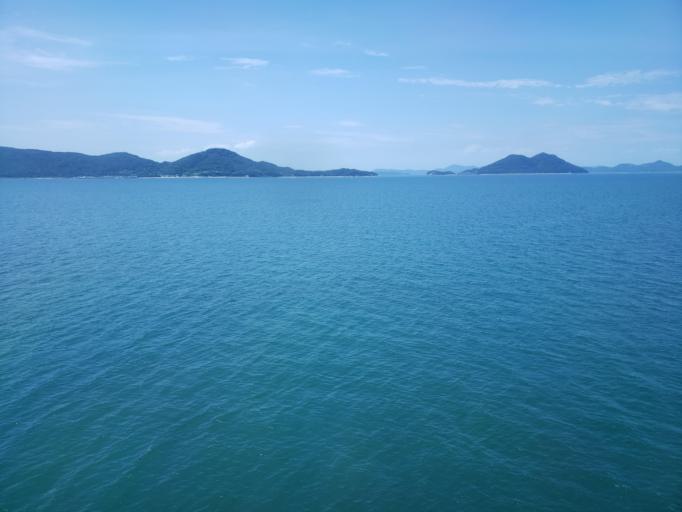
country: JP
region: Kagawa
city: Takamatsu-shi
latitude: 34.3772
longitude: 134.0833
